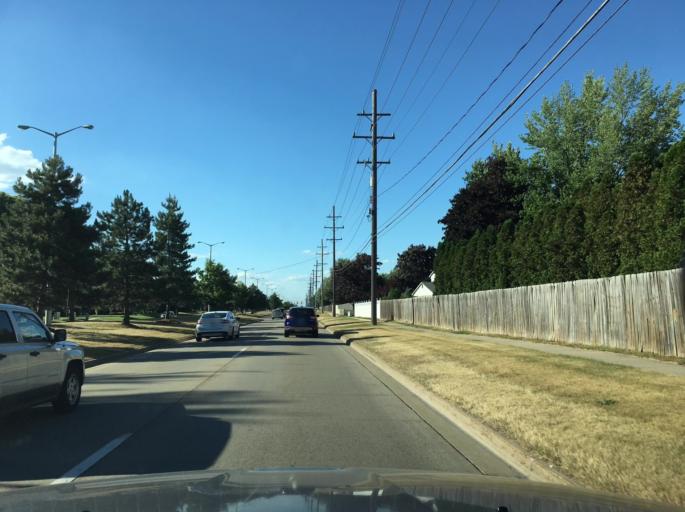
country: US
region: Michigan
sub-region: Macomb County
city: Sterling Heights
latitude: 42.6059
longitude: -82.9918
